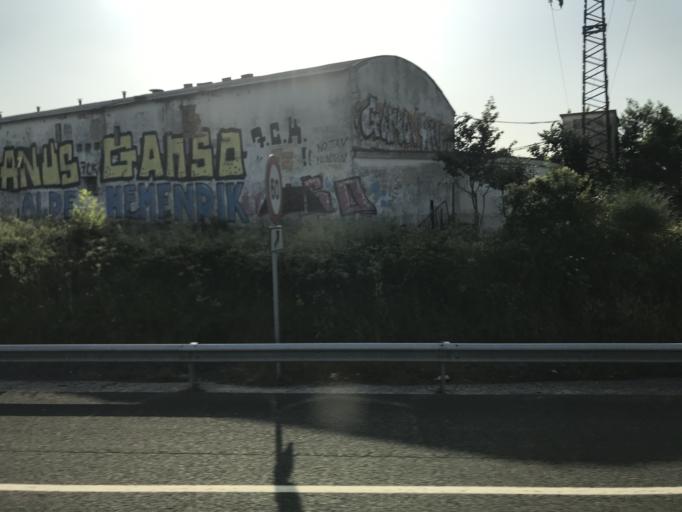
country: ES
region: Navarre
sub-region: Provincia de Navarra
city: Altsasu
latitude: 42.8999
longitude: -2.1755
